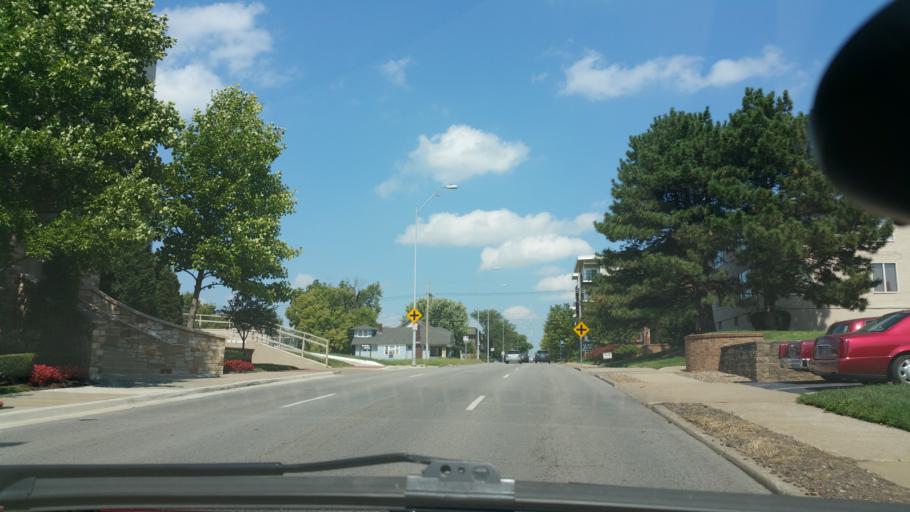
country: US
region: Kansas
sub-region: Johnson County
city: Westwood
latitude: 39.0450
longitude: -94.5972
